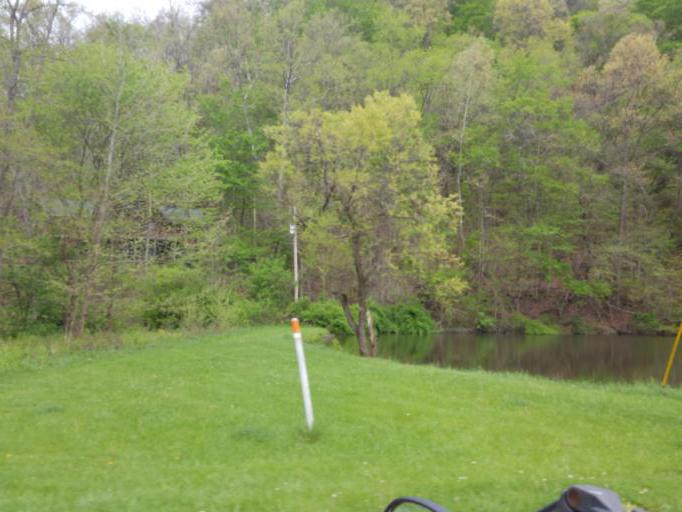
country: US
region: Ohio
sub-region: Ashland County
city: Loudonville
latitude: 40.5847
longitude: -82.1913
